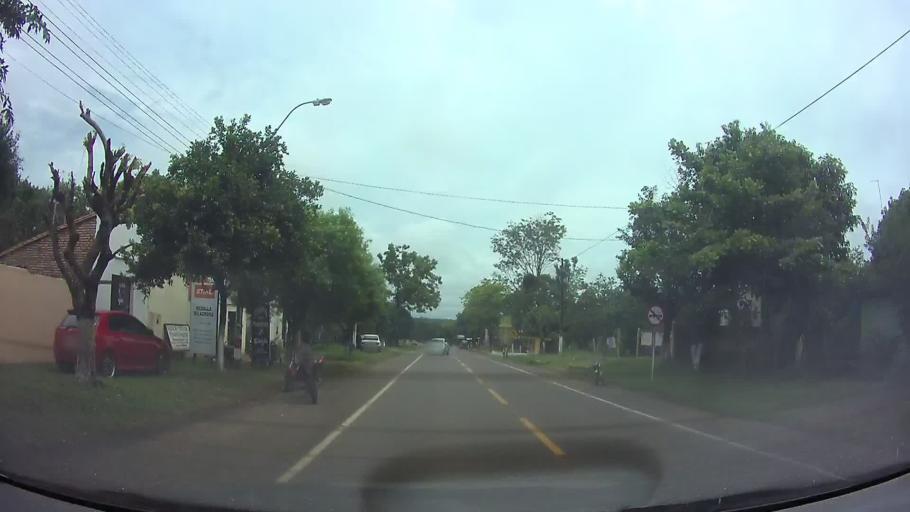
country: PY
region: Paraguari
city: Acahay
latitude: -25.9086
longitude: -57.1145
